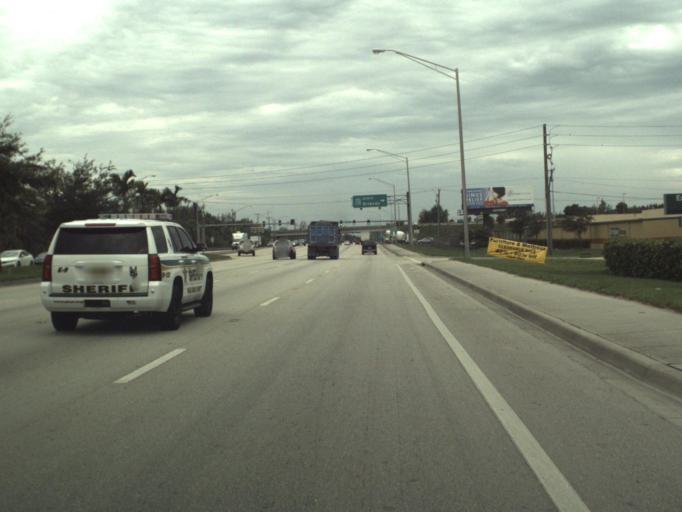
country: US
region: Florida
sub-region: Palm Beach County
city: Lake Belvedere Estates
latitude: 26.6793
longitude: -80.1609
